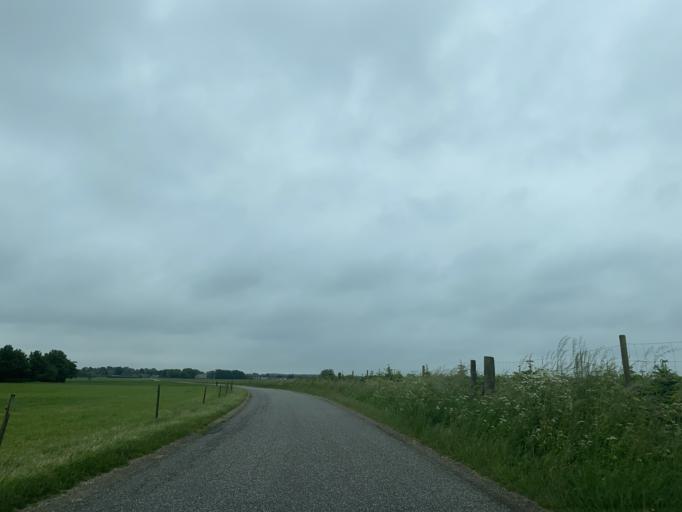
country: DK
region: Central Jutland
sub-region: Viborg Kommune
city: Bjerringbro
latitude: 56.3454
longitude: 9.6318
